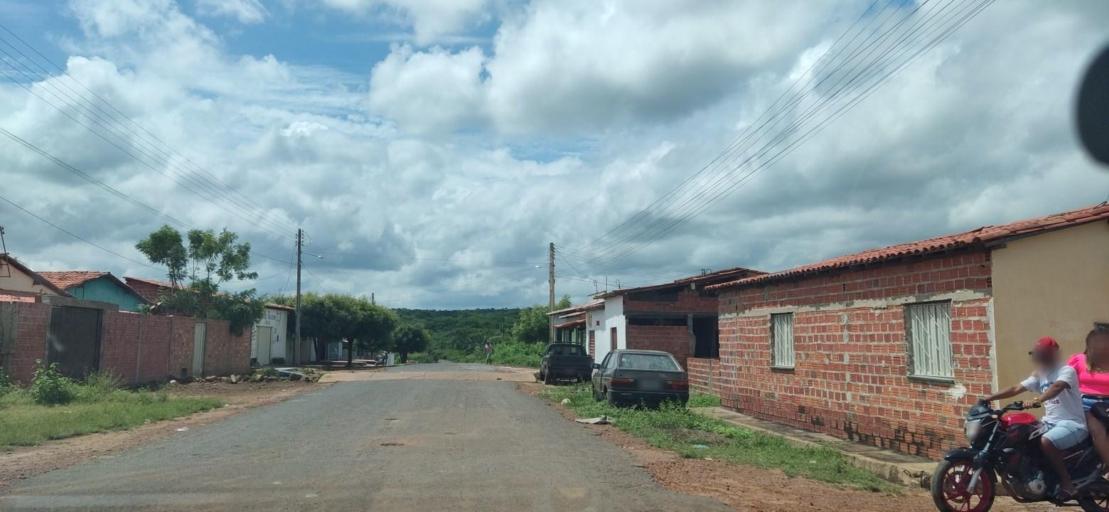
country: BR
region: Piaui
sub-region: Valenca Do Piaui
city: Valenca do Piaui
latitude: -6.4170
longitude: -41.7279
